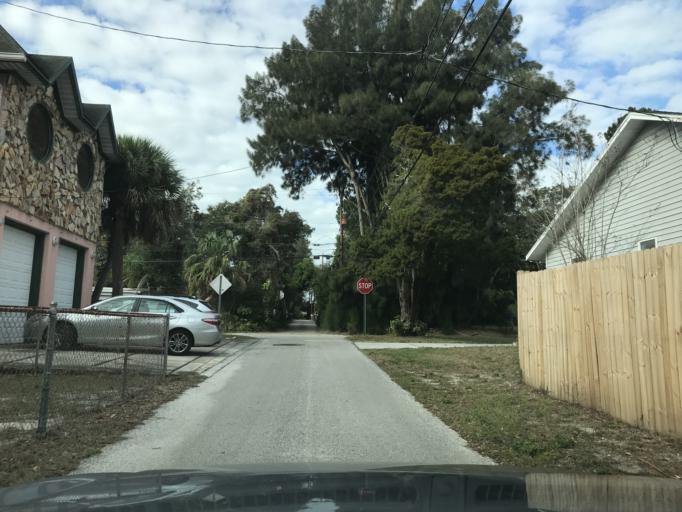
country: US
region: Florida
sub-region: Pinellas County
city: Largo
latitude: 27.9235
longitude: -82.7809
